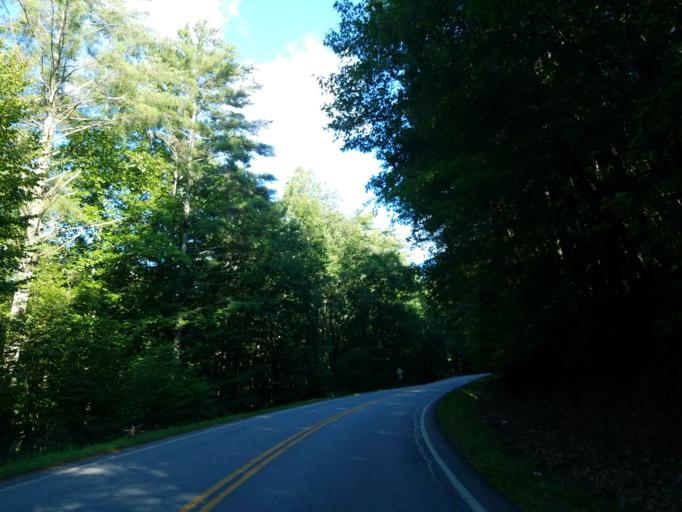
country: US
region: Georgia
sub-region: Fannin County
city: Blue Ridge
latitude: 34.7481
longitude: -84.1436
